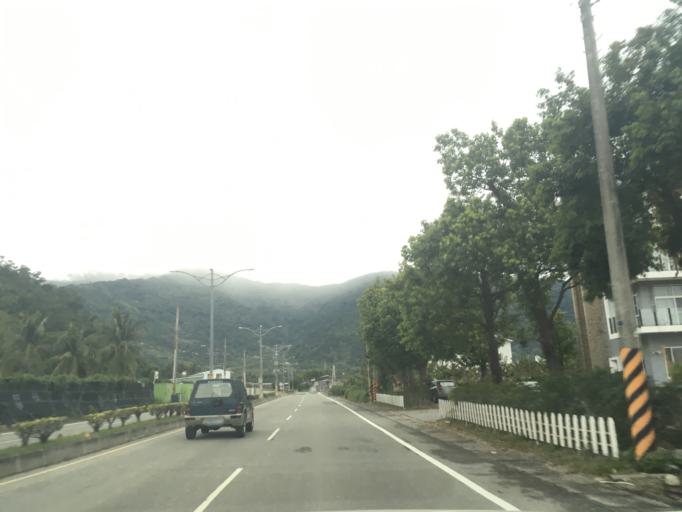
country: TW
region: Taiwan
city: Taitung City
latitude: 22.6972
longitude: 121.0433
